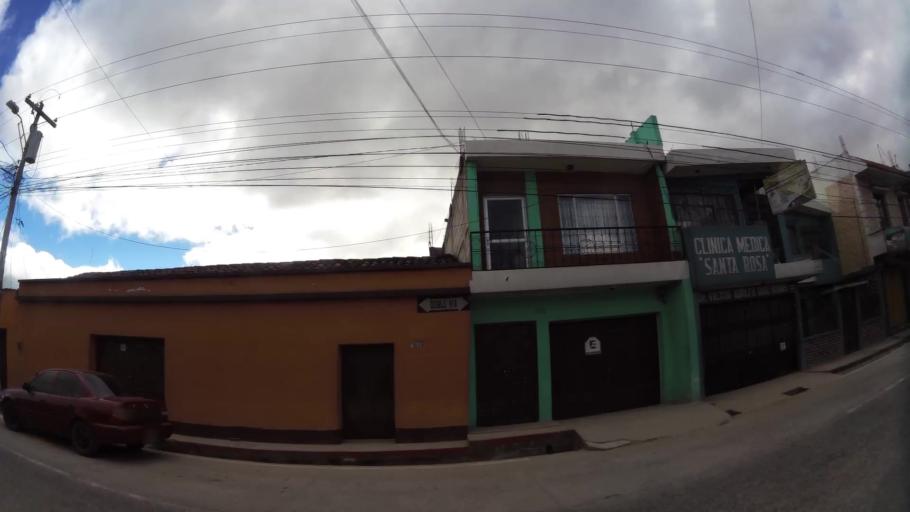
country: GT
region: Quetzaltenango
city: Salcaja
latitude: 14.8750
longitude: -91.4632
